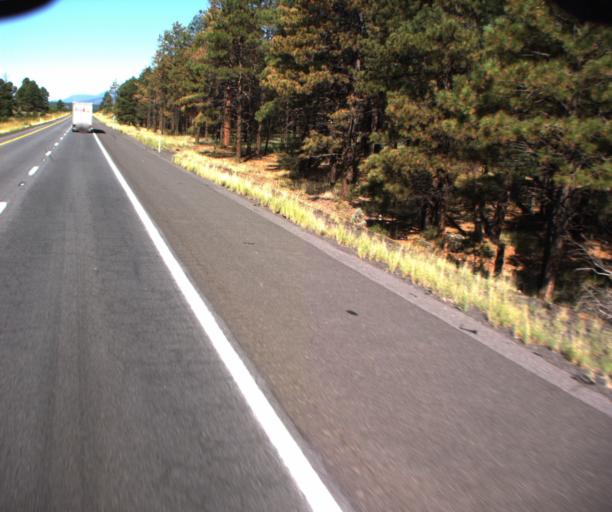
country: US
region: Arizona
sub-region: Coconino County
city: Parks
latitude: 35.2512
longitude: -111.9580
